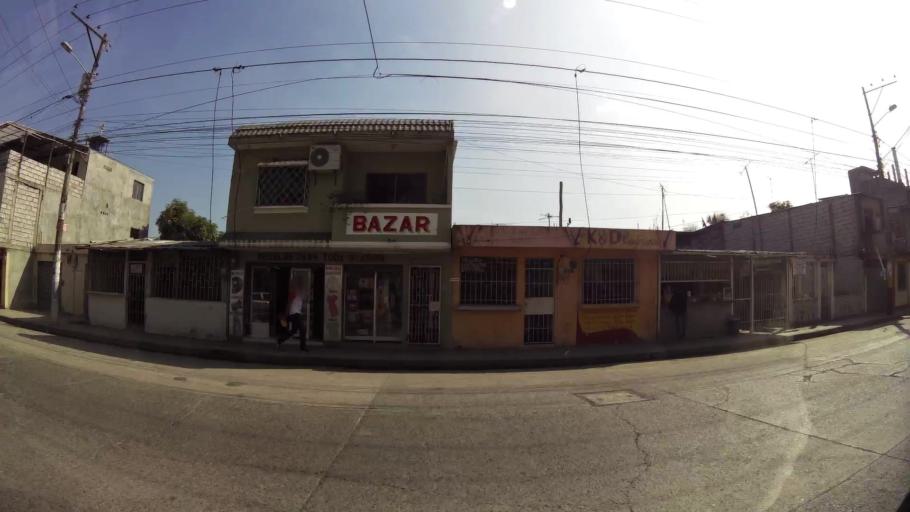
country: EC
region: Guayas
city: Eloy Alfaro
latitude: -2.1687
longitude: -79.7997
